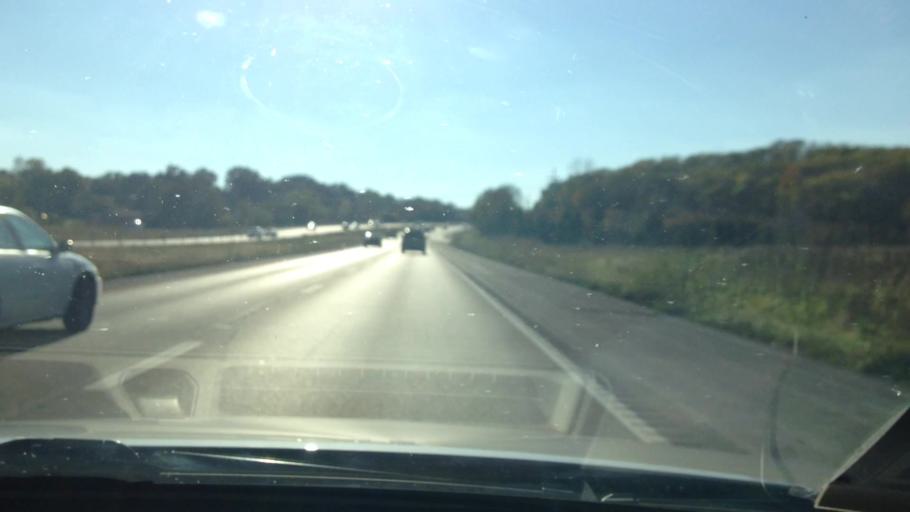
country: US
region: Missouri
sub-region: Clay County
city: Gladstone
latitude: 39.2560
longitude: -94.6027
